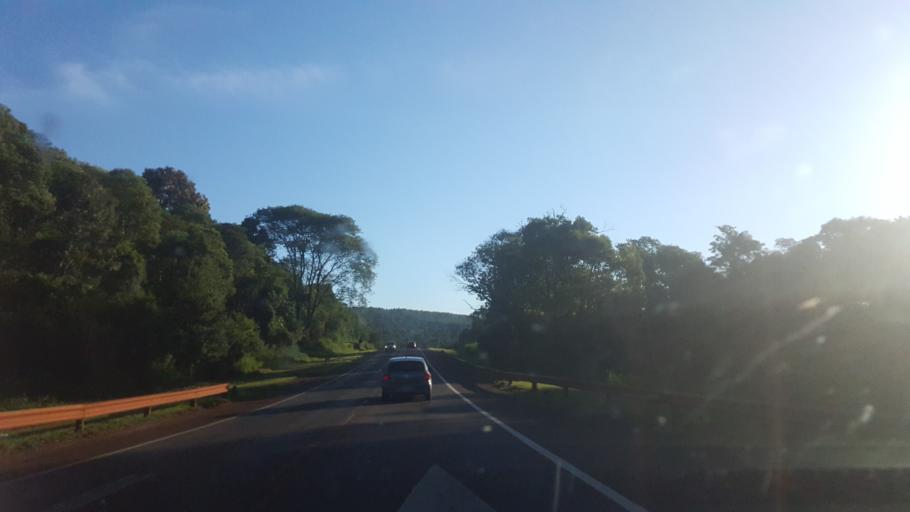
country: AR
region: Misiones
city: El Alcazar
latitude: -26.7159
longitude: -54.8533
